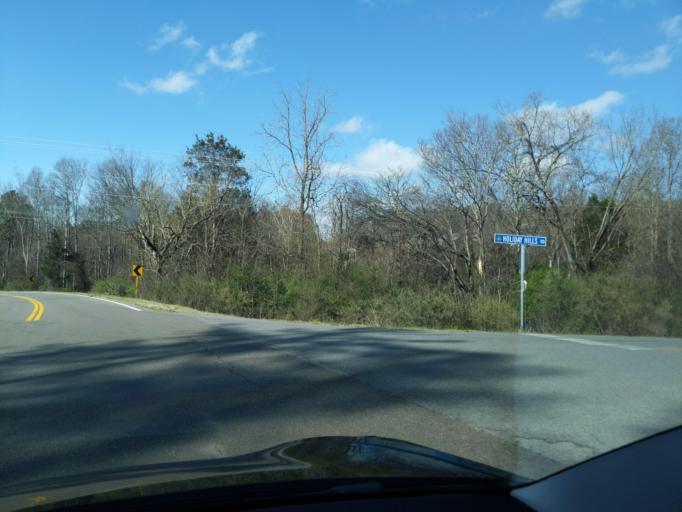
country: US
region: Tennessee
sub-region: Sevier County
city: Sevierville
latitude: 35.9653
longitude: -83.5475
